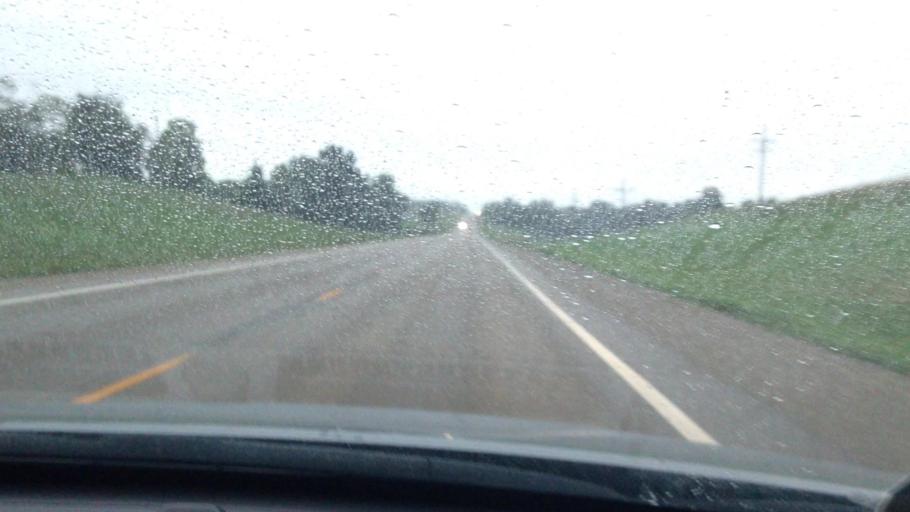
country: US
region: Kansas
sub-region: Brown County
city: Hiawatha
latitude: 39.8298
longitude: -95.5270
